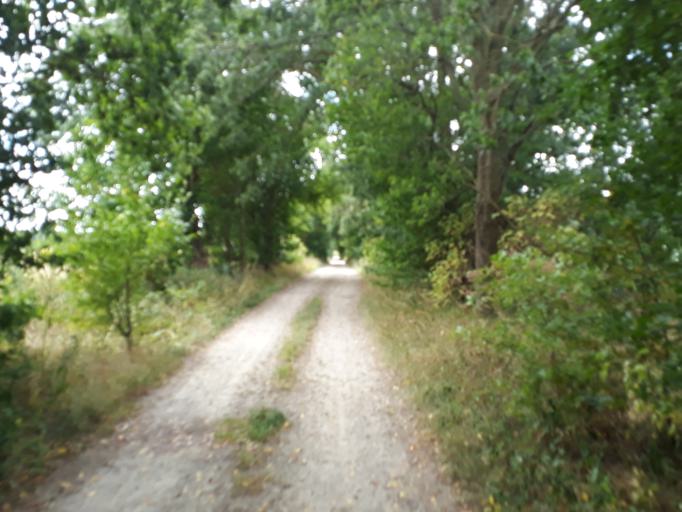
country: DE
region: Mecklenburg-Vorpommern
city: Marlow
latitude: 54.1778
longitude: 12.6052
